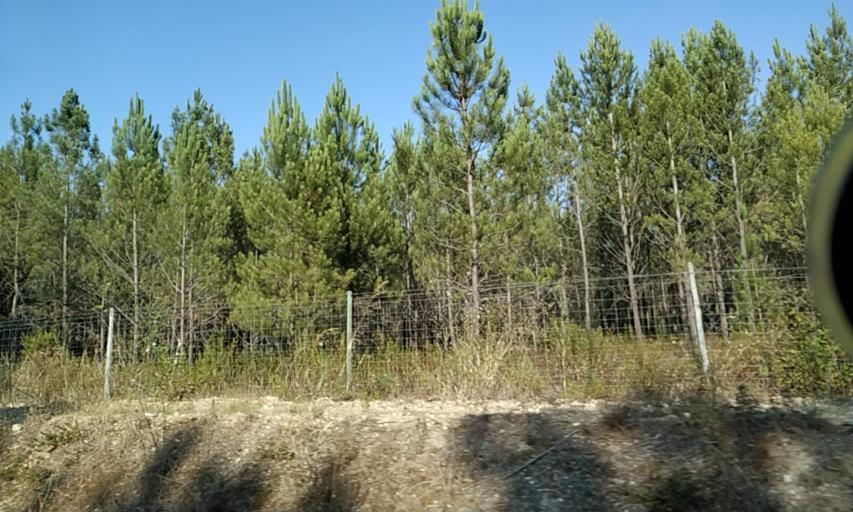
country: PT
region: Santarem
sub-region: Coruche
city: Coruche
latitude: 39.0249
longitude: -8.5625
